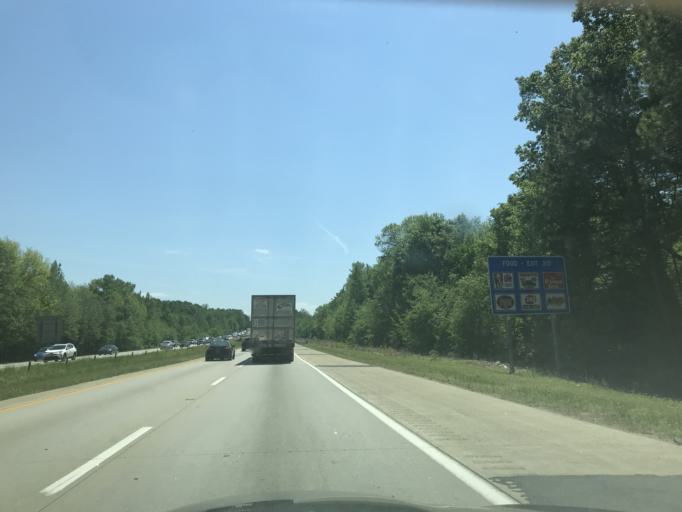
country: US
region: North Carolina
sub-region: Wake County
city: Garner
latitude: 35.6242
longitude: -78.5670
